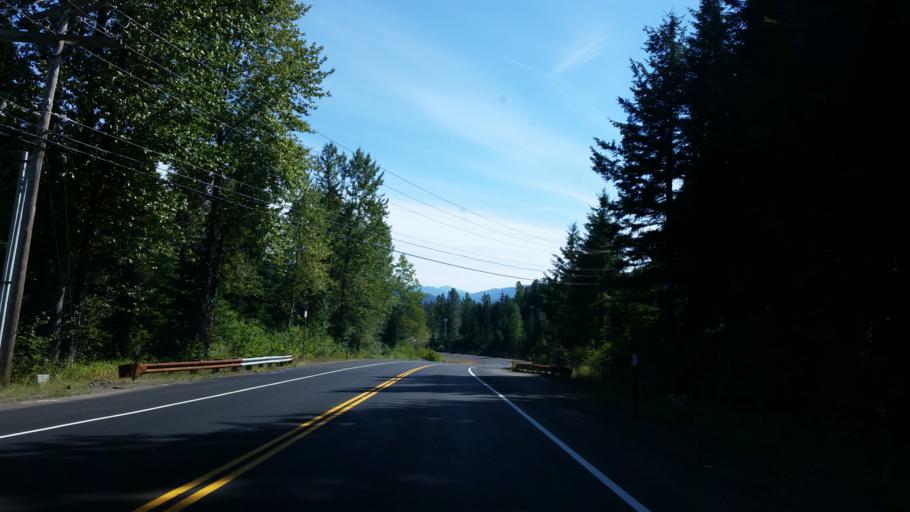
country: US
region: Washington
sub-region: King County
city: Tanner
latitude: 47.3979
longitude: -121.4005
